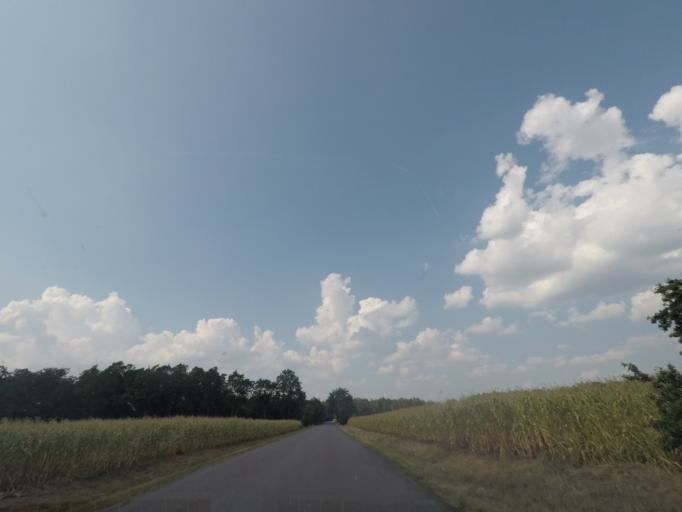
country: CZ
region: Pardubicky
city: Horni Jeleni
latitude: 50.0559
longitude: 16.0828
